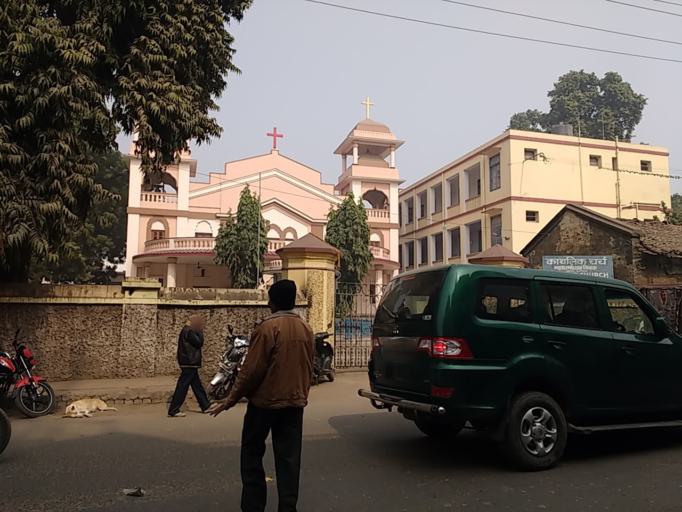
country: IN
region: Bihar
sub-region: Patna
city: Patna
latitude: 25.6195
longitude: 85.1542
